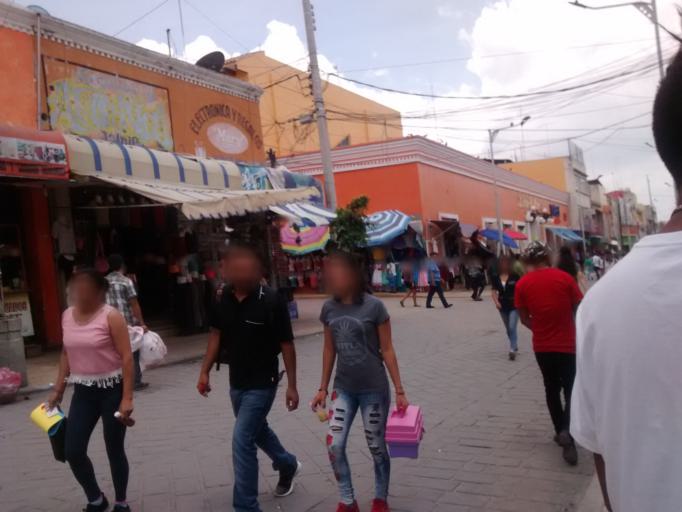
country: MX
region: Puebla
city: Tehuacan
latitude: 18.4618
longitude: -97.3908
